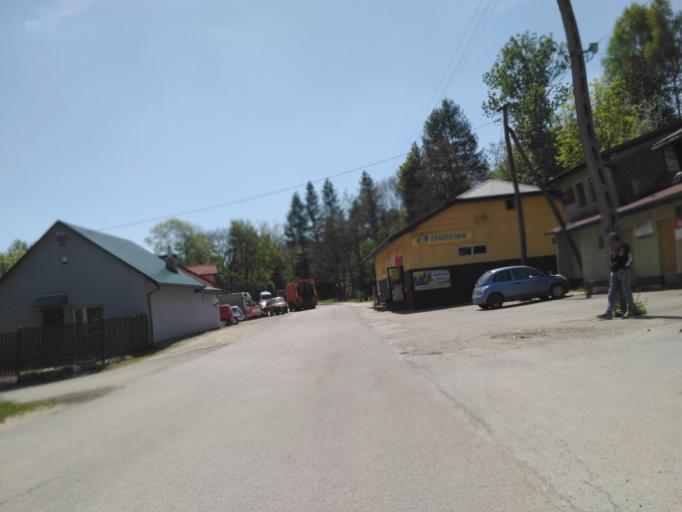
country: PL
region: Subcarpathian Voivodeship
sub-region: Powiat krosnienski
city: Iwonicz-Zdroj
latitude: 49.5424
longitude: 21.7612
